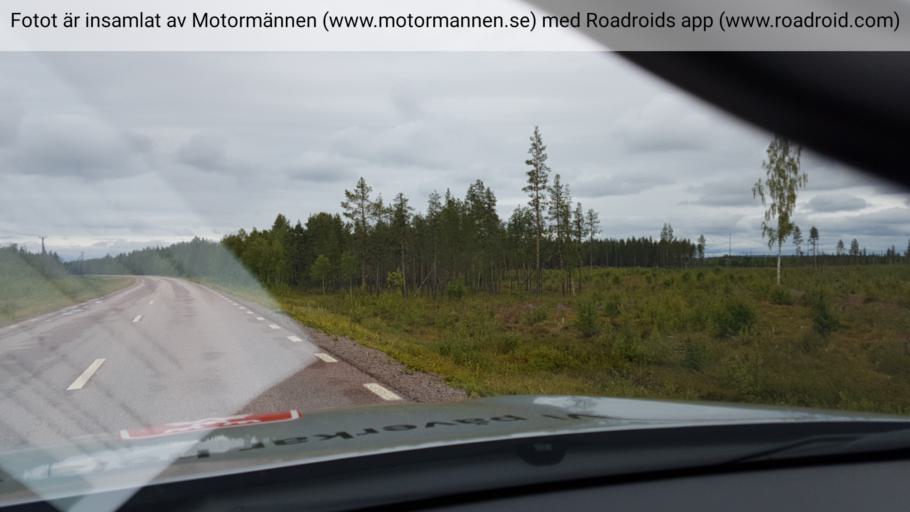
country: SE
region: Norrbotten
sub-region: Pajala Kommun
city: Pajala
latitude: 67.1061
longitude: 22.5967
